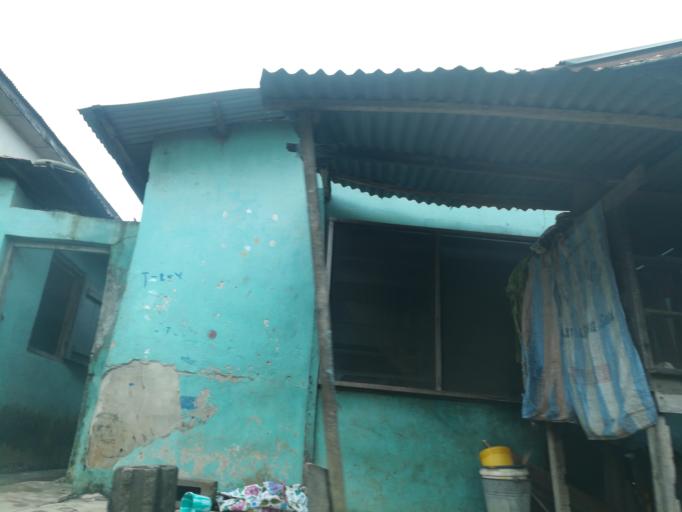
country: NG
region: Lagos
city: Agege
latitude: 6.6090
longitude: 3.3212
